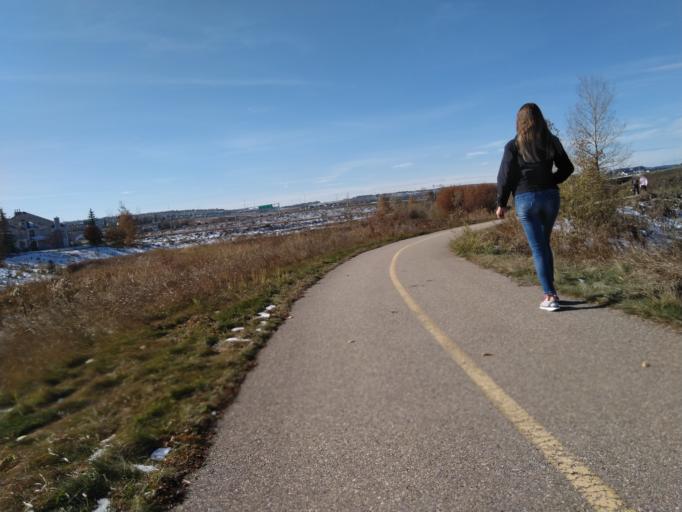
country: CA
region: Alberta
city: Calgary
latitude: 51.1569
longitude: -114.1054
